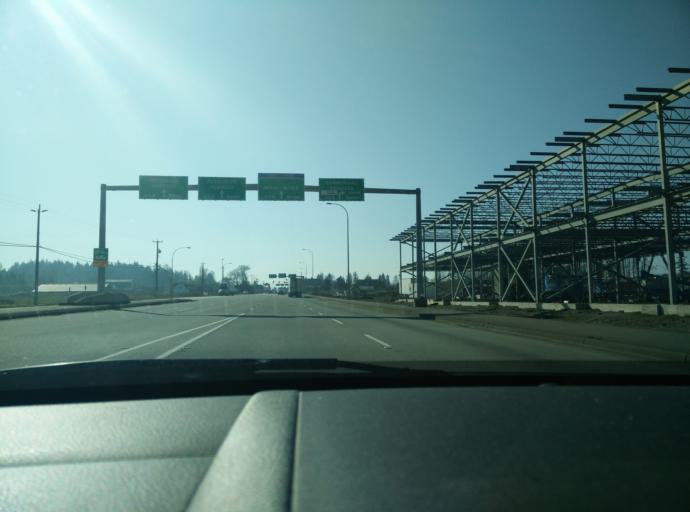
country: US
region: Washington
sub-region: Whatcom County
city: Blaine
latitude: 49.0086
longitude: -122.7356
